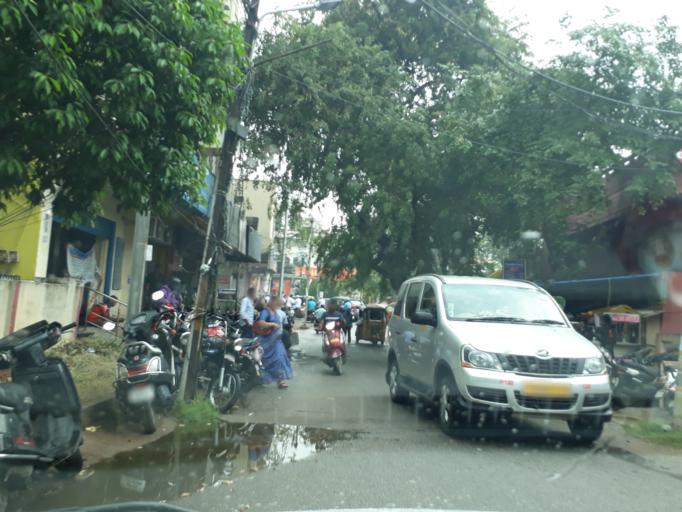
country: IN
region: Telangana
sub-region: Hyderabad
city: Malkajgiri
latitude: 17.4609
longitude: 78.5008
